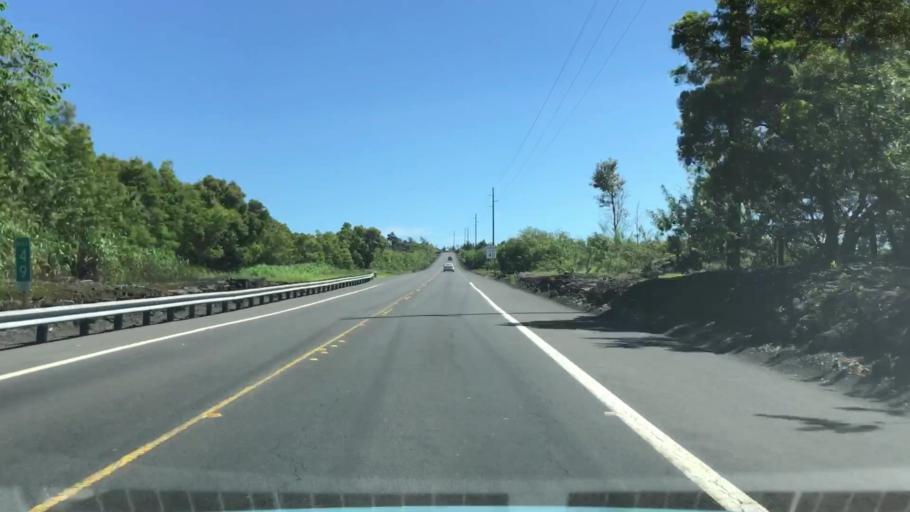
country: US
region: Hawaii
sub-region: Hawaii County
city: Pahala
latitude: 19.2302
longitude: -155.4555
